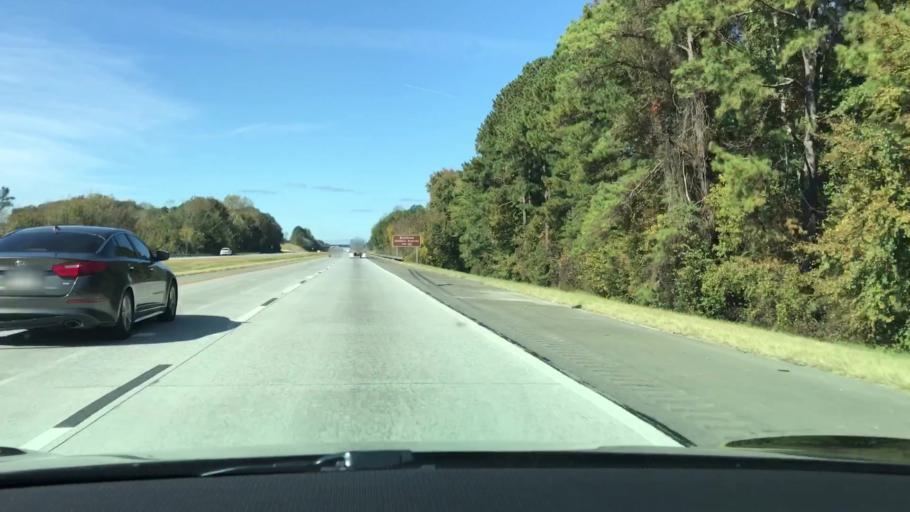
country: US
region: Georgia
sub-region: Putnam County
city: Jefferson
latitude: 33.5483
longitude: -83.3460
